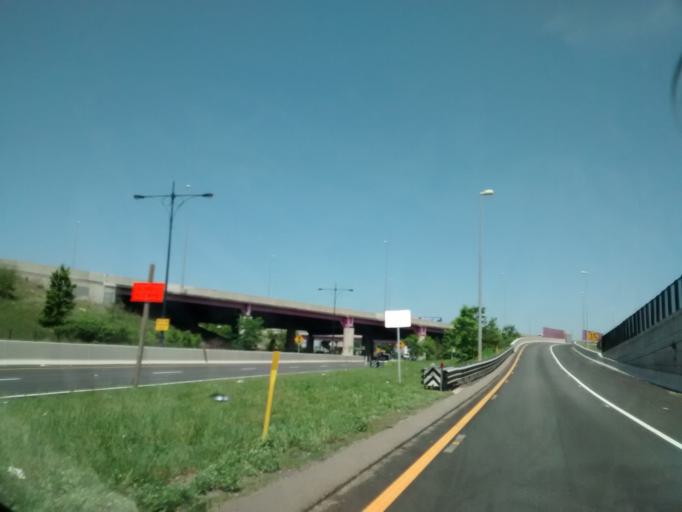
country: US
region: Massachusetts
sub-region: Worcester County
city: Worcester
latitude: 42.2436
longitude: -71.8026
